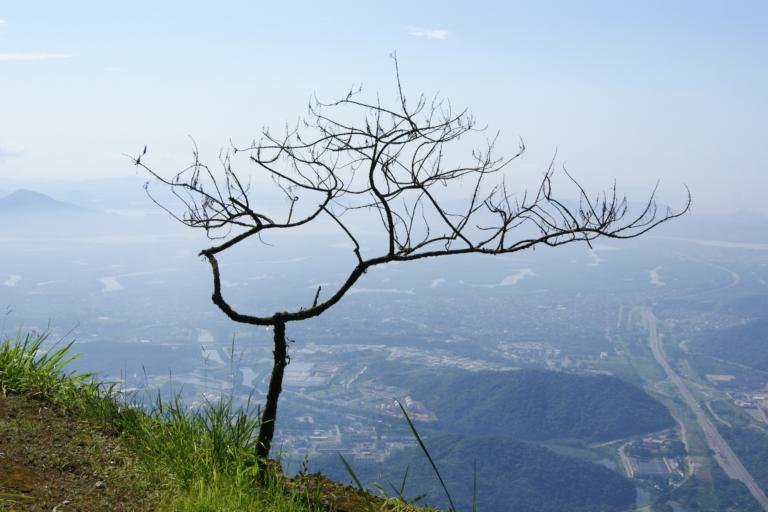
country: BR
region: Sao Paulo
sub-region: Cubatao
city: Cubatao
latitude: -23.8665
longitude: -46.4600
